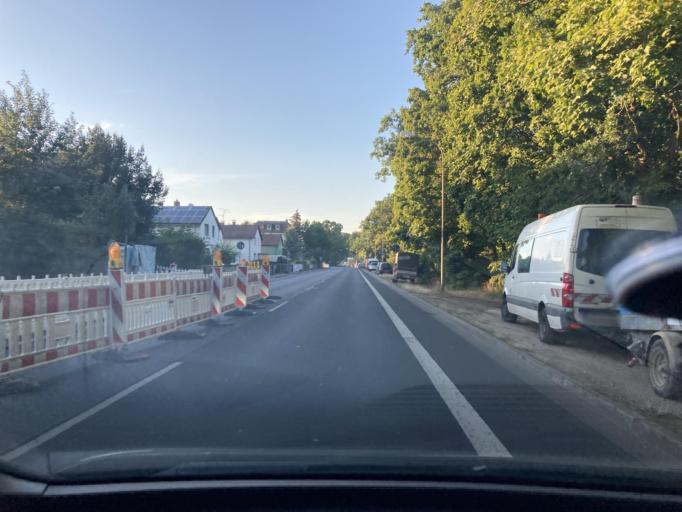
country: DE
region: Hesse
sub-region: Regierungsbezirk Darmstadt
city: Offenbach
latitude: 50.0749
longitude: 8.7659
